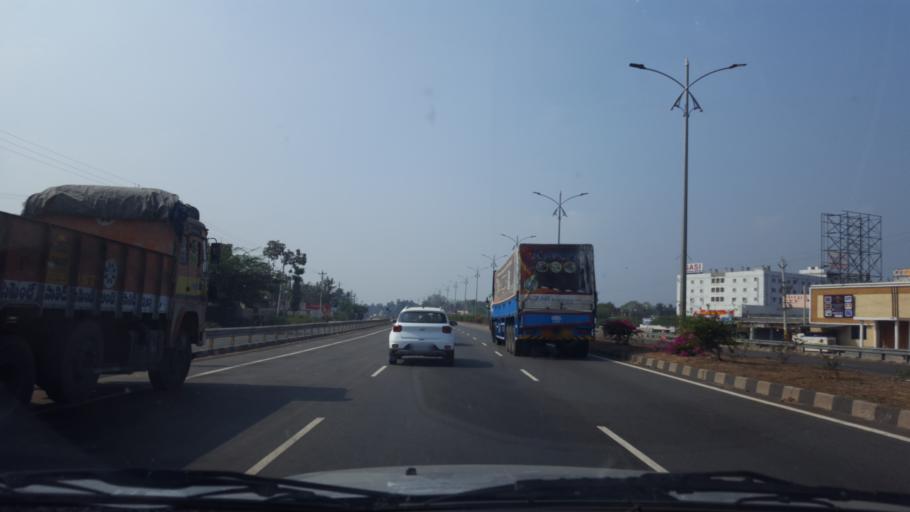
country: IN
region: Andhra Pradesh
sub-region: Vishakhapatnam
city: Bhimunipatnam
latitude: 17.9195
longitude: 83.4167
